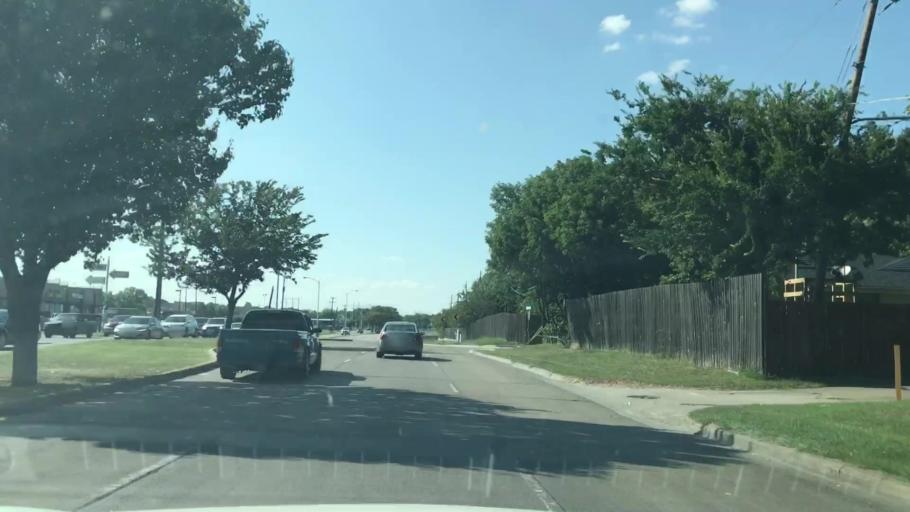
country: US
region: Texas
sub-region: Dallas County
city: Garland
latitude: 32.8305
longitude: -96.6543
